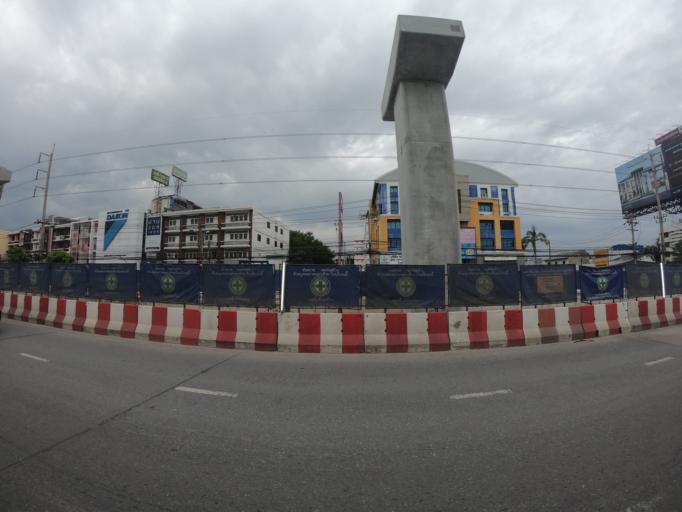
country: TH
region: Bangkok
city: Suan Luang
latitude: 13.7025
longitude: 100.6460
